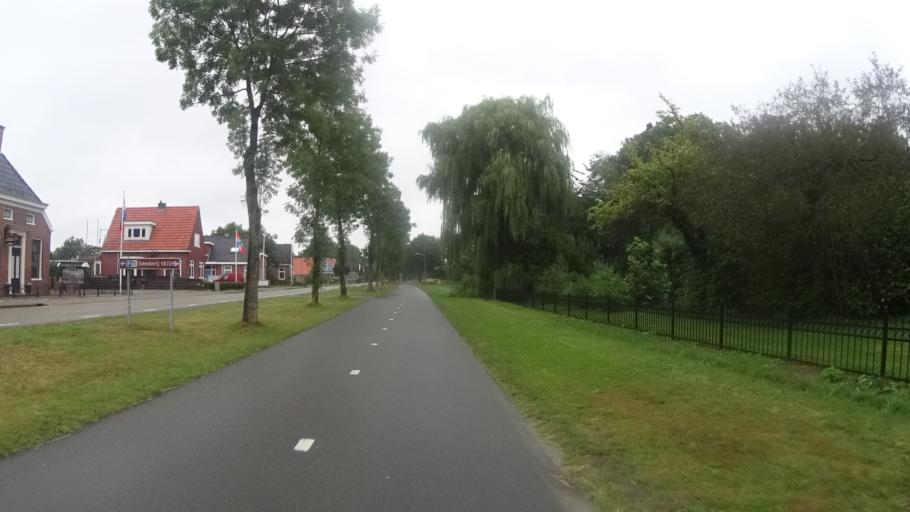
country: NL
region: Groningen
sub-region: Gemeente  Oldambt
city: Winschoten
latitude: 53.1628
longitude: 7.0833
